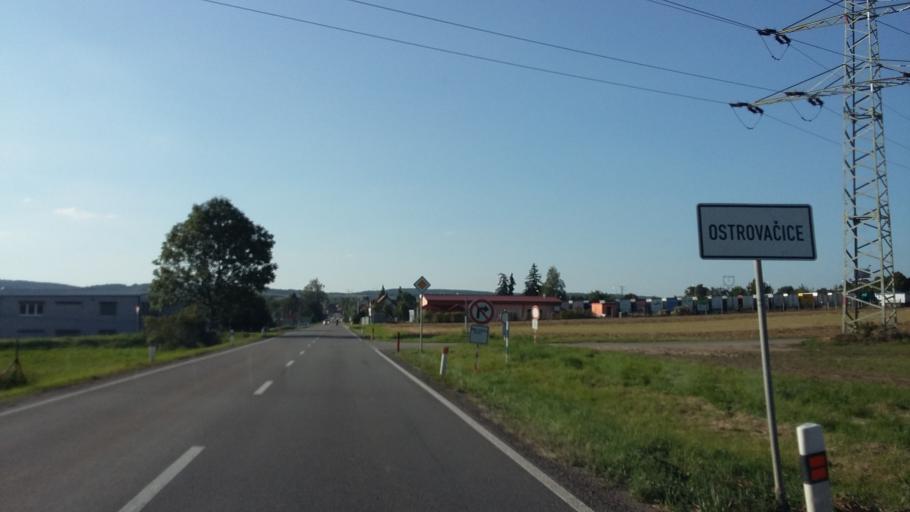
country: CZ
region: South Moravian
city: Ricany
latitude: 49.2036
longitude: 16.4186
